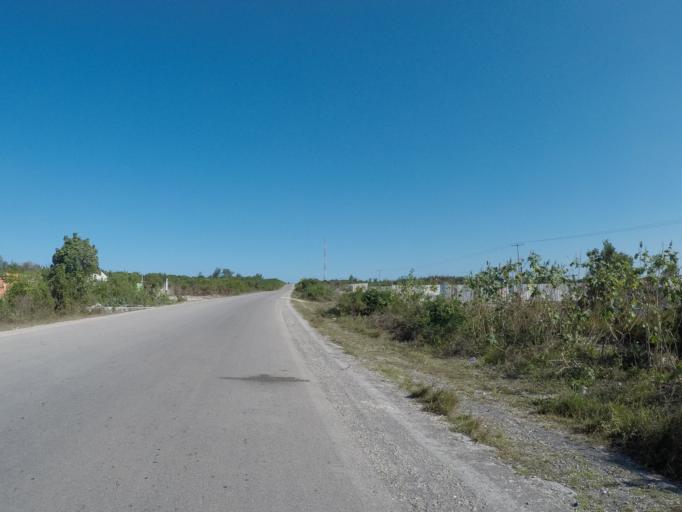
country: TZ
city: Kiwengwa
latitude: -6.1547
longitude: 39.5181
